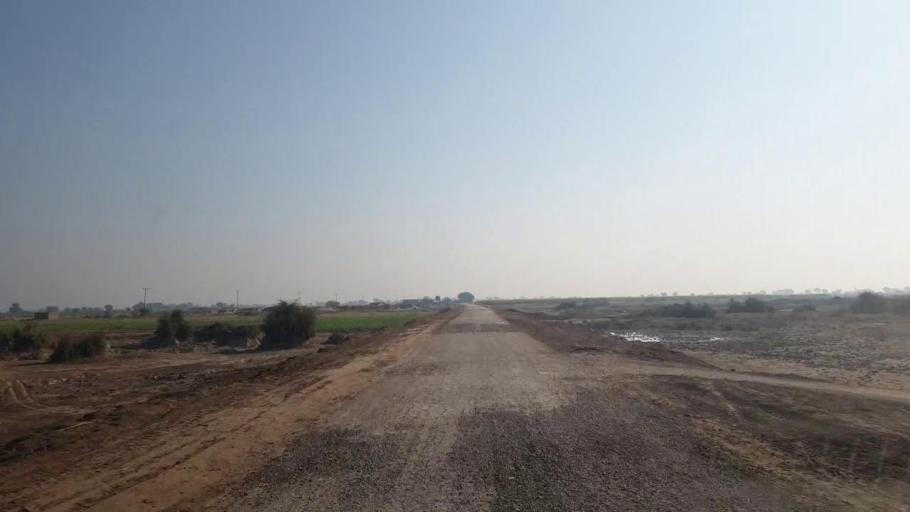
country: PK
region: Sindh
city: Shahpur Chakar
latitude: 26.0658
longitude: 68.5926
